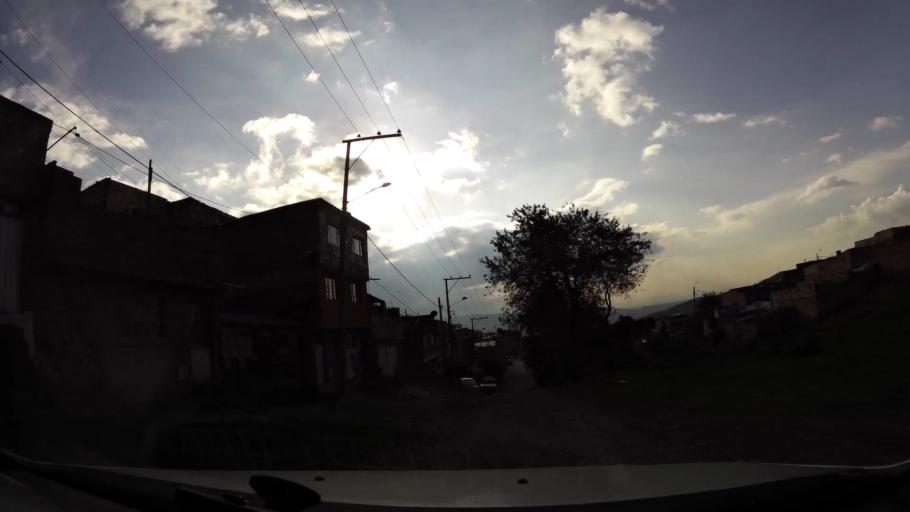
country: CO
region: Bogota D.C.
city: Bogota
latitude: 4.5427
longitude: -74.0904
